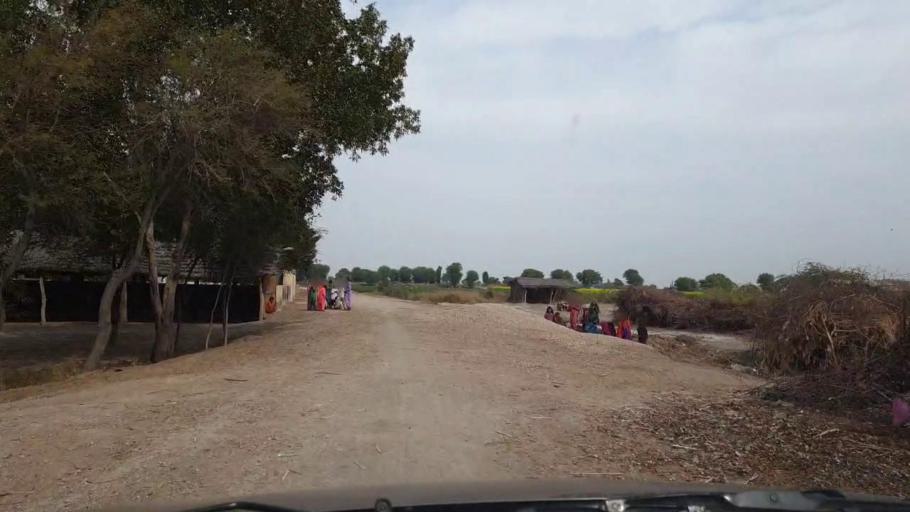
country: PK
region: Sindh
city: Sanghar
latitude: 26.0963
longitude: 68.8814
